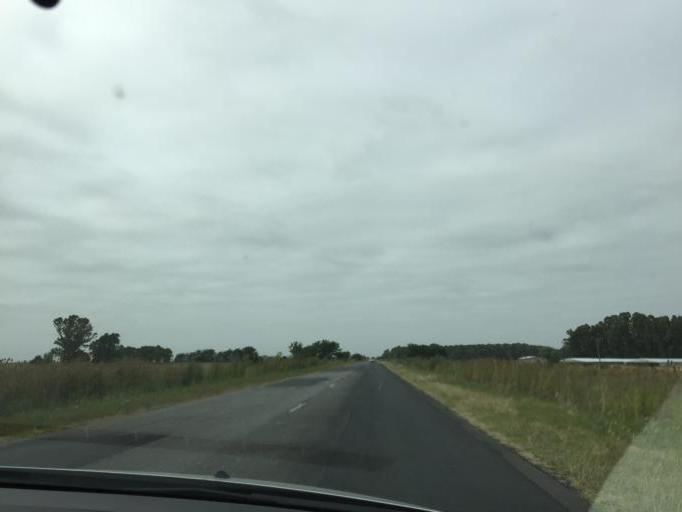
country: AR
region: Buenos Aires
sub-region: Partido de Las Flores
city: Las Flores
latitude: -36.2173
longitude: -59.0448
